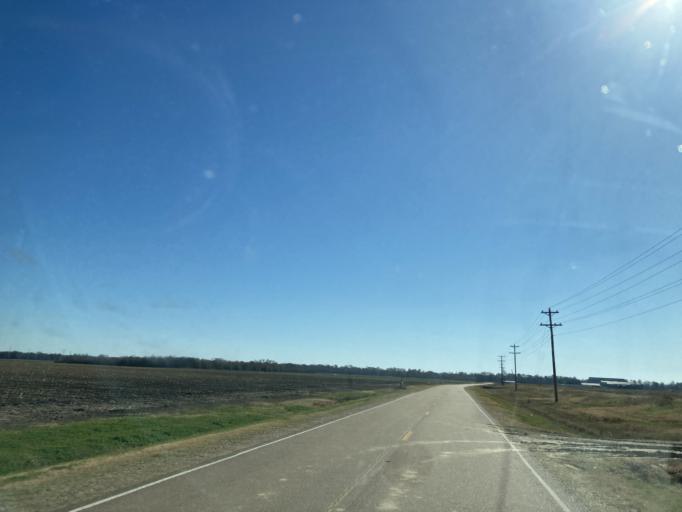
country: US
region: Mississippi
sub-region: Yazoo County
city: Yazoo City
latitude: 32.9135
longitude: -90.4465
